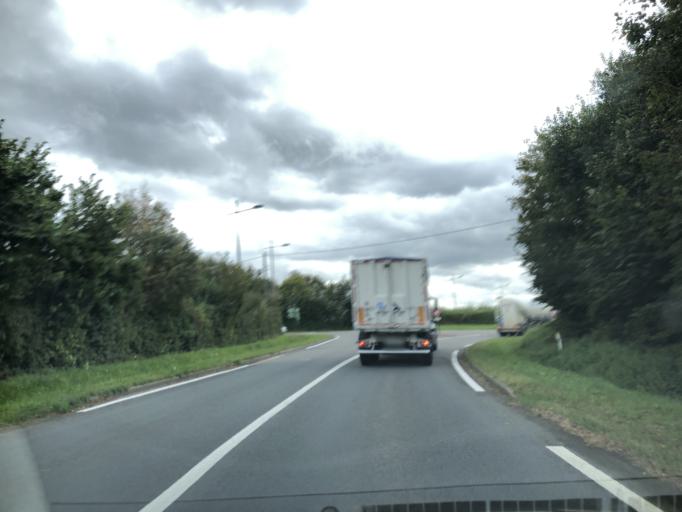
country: FR
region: Nord-Pas-de-Calais
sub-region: Departement du Pas-de-Calais
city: Wailly
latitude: 50.5561
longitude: 2.0982
